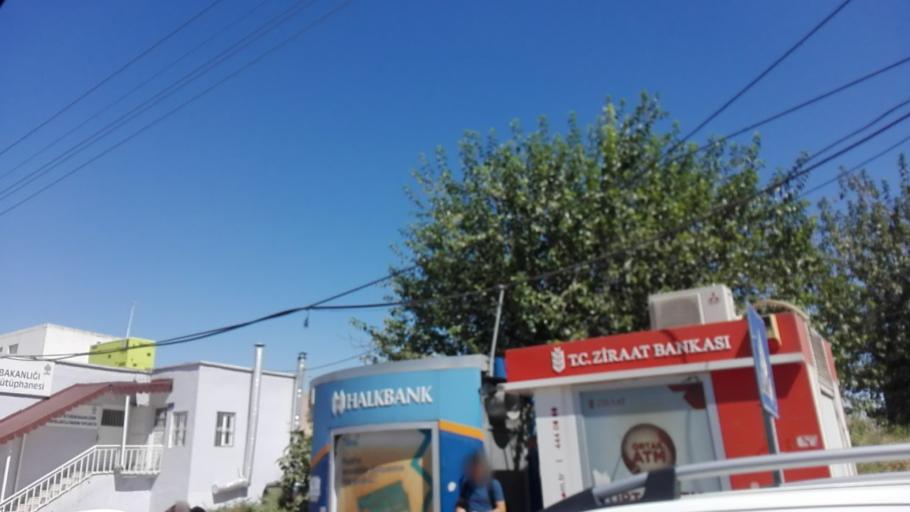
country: TR
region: Batman
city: Hasankeyf
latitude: 37.7138
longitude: 41.4137
